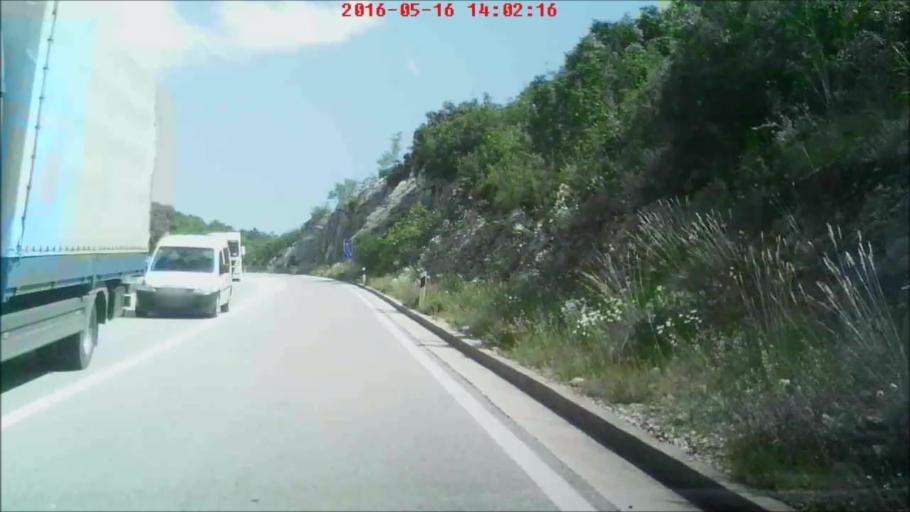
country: HR
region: Dubrovacko-Neretvanska
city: Ston
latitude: 42.8261
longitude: 17.7565
